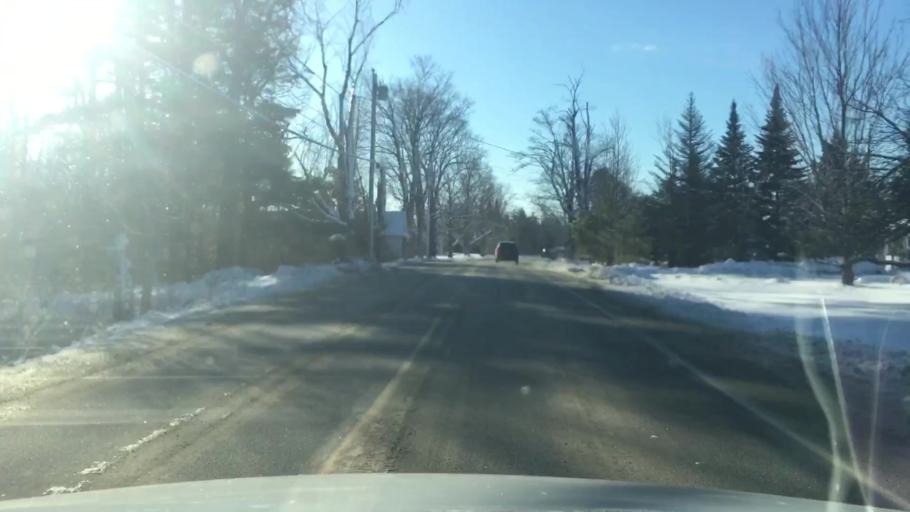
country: US
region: Maine
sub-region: Kennebec County
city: Readfield
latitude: 44.4015
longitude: -69.9632
